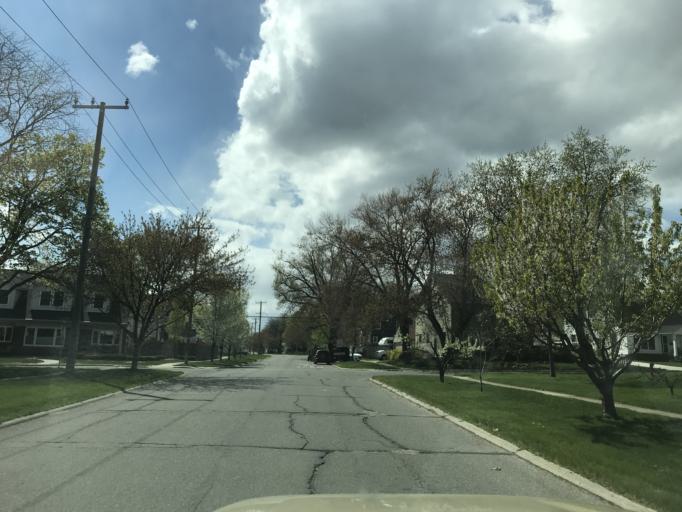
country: US
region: Michigan
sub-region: Wayne County
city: Plymouth
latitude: 42.3777
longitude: -83.4738
